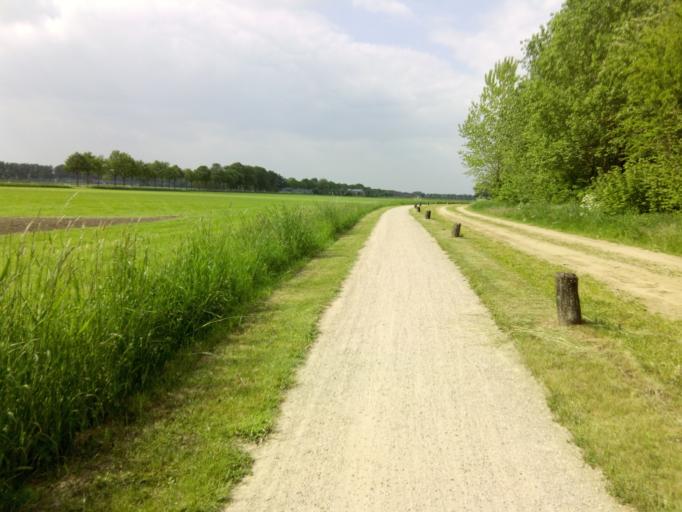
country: NL
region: Gelderland
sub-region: Berkelland
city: Borculo
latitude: 52.0524
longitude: 6.5237
